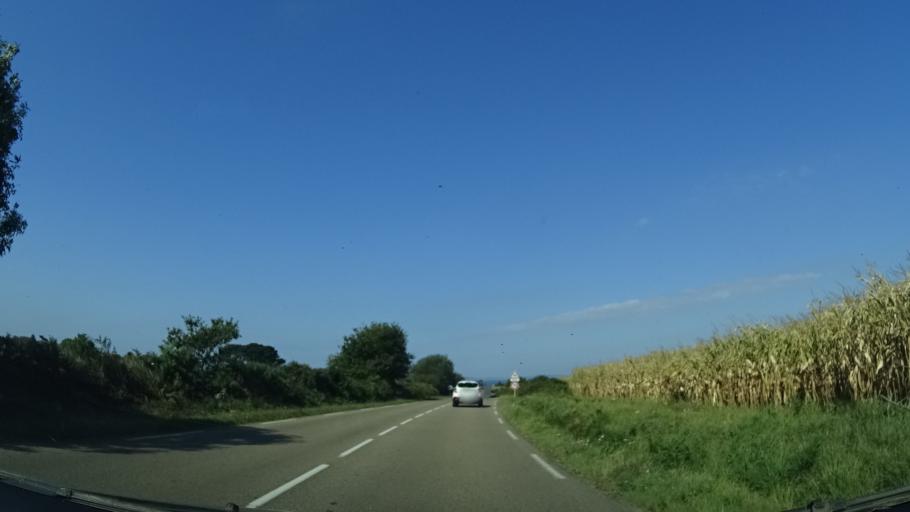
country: FR
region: Brittany
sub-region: Departement du Finistere
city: Douarnenez
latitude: 48.0925
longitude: -4.2793
